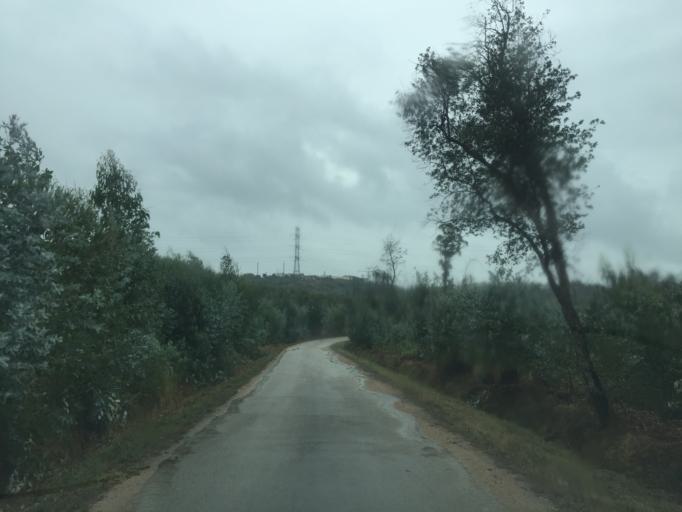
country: PT
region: Coimbra
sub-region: Figueira da Foz
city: Lavos
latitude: 40.0803
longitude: -8.7991
